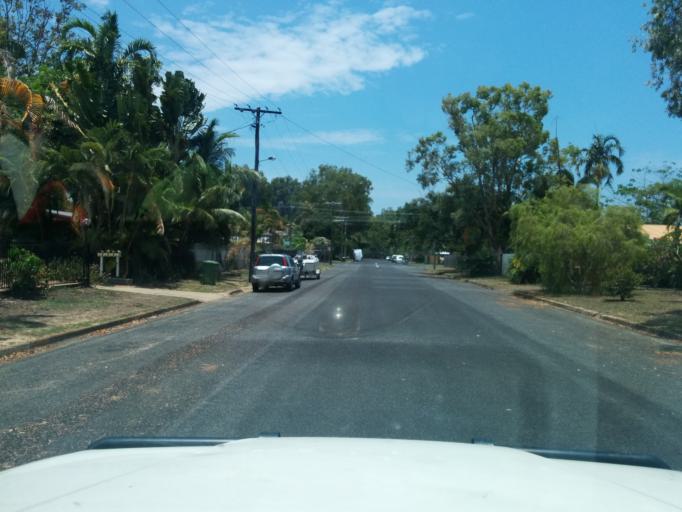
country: AU
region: Queensland
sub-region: Cairns
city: Yorkeys Knob
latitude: -16.8411
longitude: 145.7364
